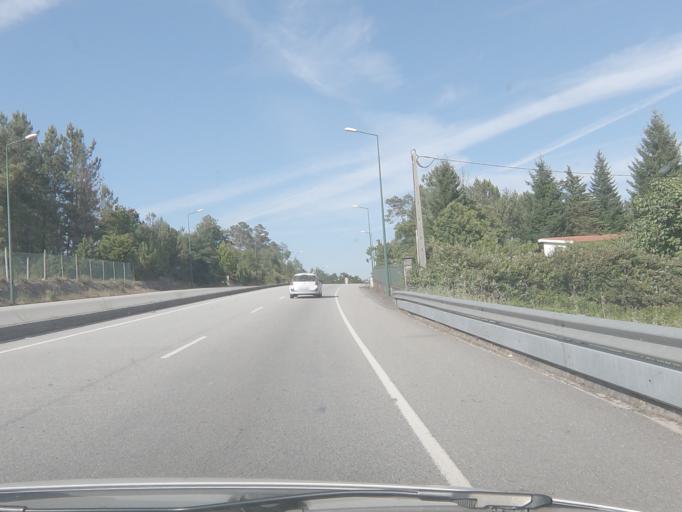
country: PT
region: Viseu
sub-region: Viseu
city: Viseu
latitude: 40.6288
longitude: -7.9390
